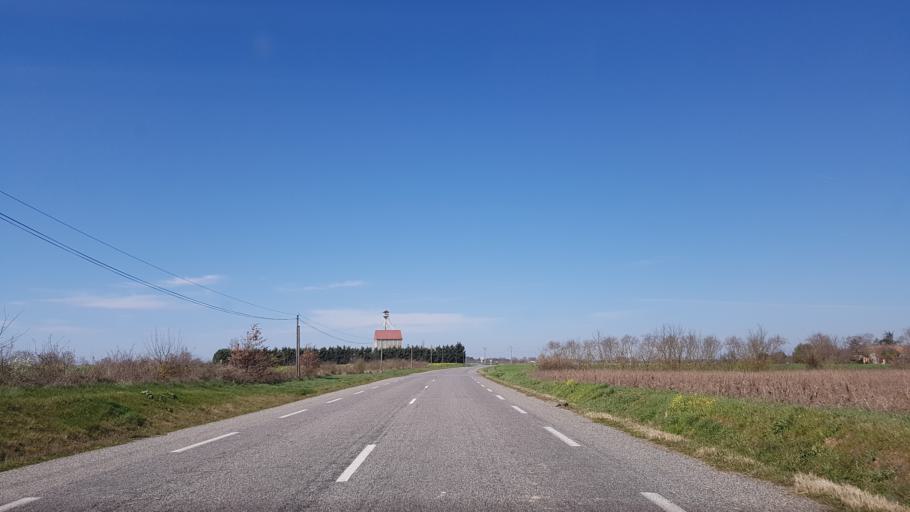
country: FR
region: Midi-Pyrenees
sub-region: Departement de l'Ariege
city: Mazeres
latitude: 43.2330
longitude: 1.6608
